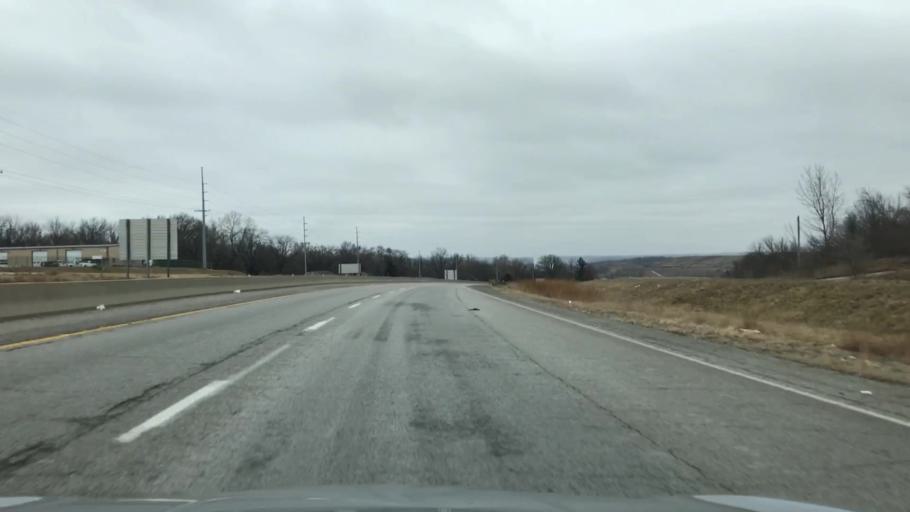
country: US
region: Missouri
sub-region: Jackson County
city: East Independence
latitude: 39.1201
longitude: -94.3860
